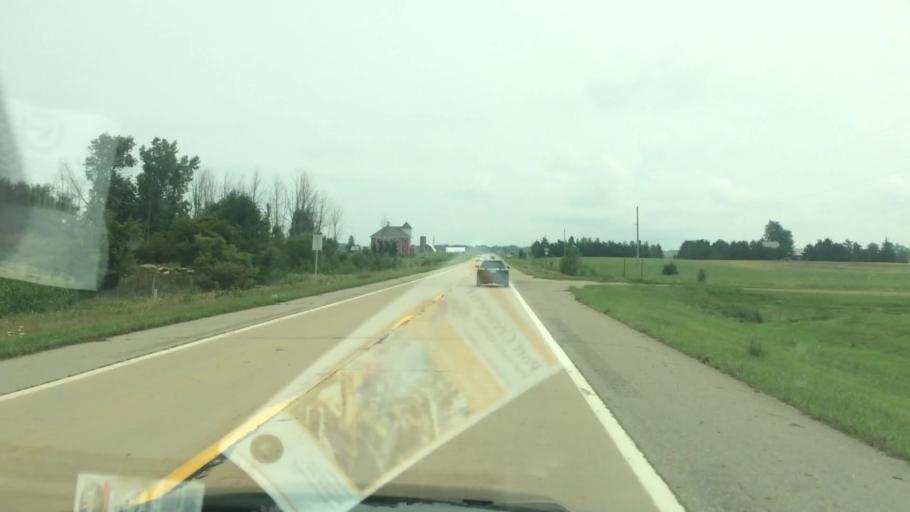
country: US
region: Michigan
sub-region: Huron County
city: Bad Axe
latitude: 44.0435
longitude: -82.9104
